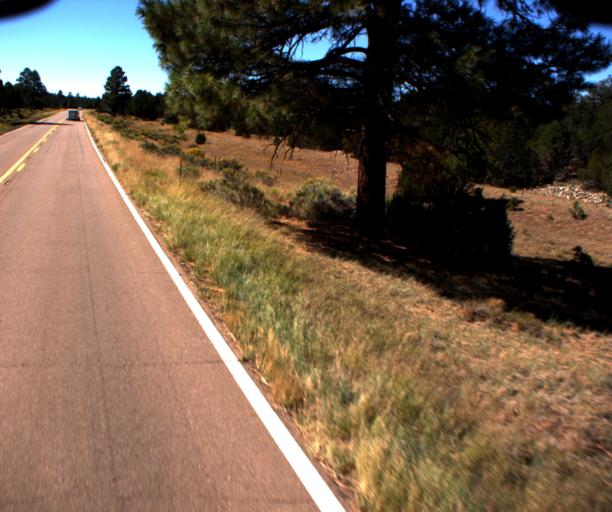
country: US
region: Arizona
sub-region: Navajo County
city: Heber-Overgaard
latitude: 34.4388
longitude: -110.5346
